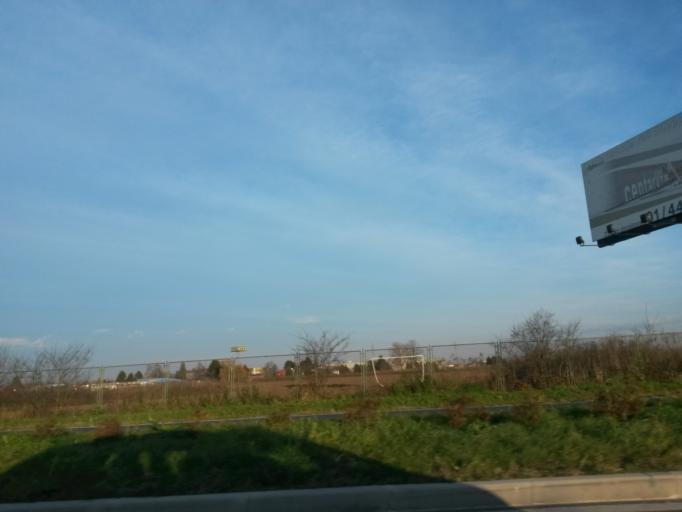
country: HR
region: Varazdinska
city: Varazdin
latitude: 46.2865
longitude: 16.3543
